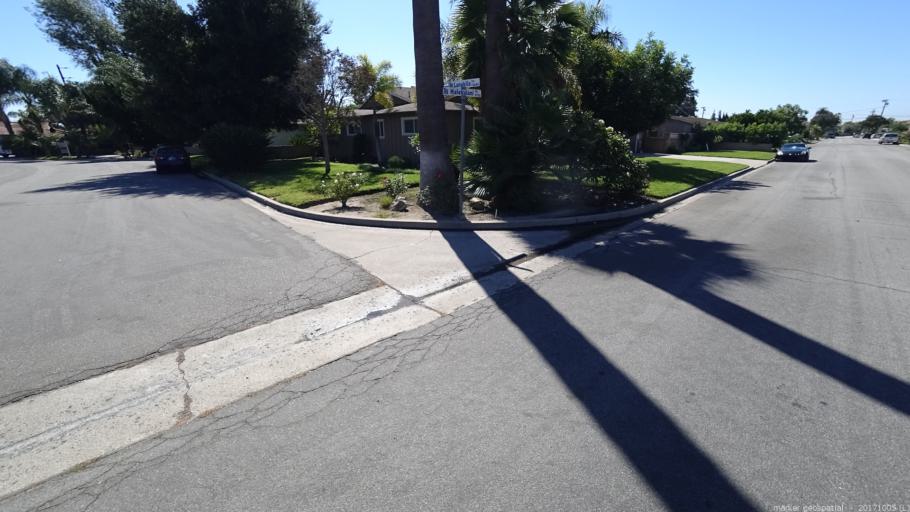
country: US
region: California
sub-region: Orange County
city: Garden Grove
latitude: 33.7790
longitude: -117.9632
